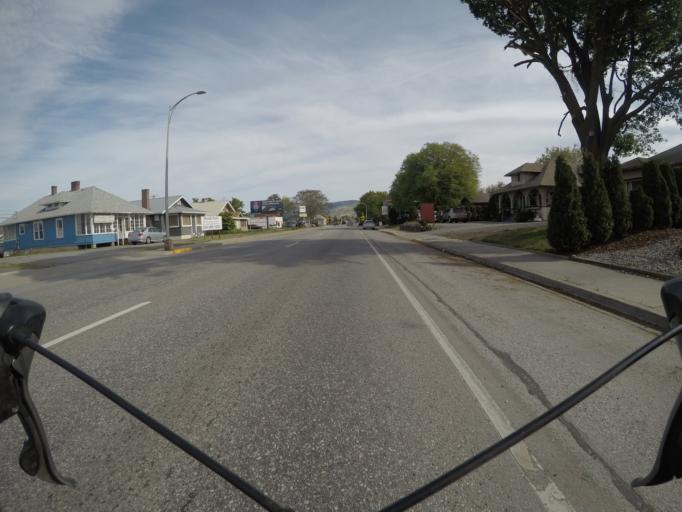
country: US
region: Washington
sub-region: Chelan County
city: Wenatchee
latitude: 47.4185
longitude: -120.3096
